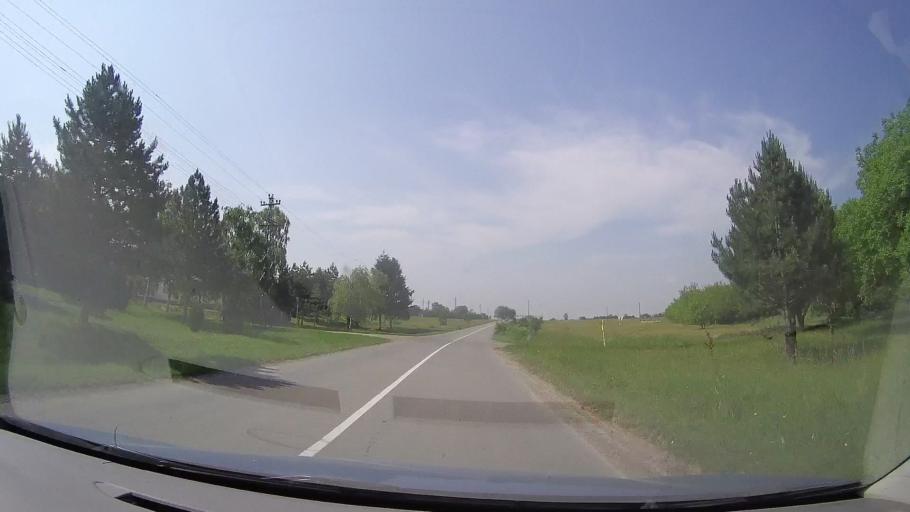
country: RS
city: Samos
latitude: 45.1981
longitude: 20.7713
